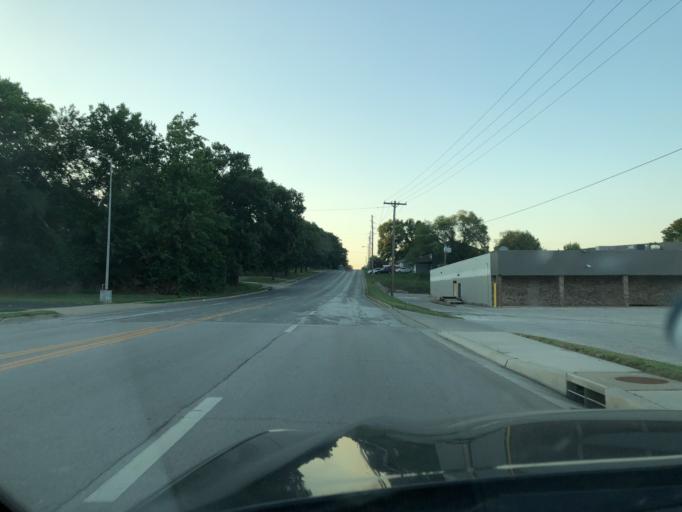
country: US
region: Kansas
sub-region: Leavenworth County
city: Leavenworth
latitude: 39.3108
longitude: -94.9507
